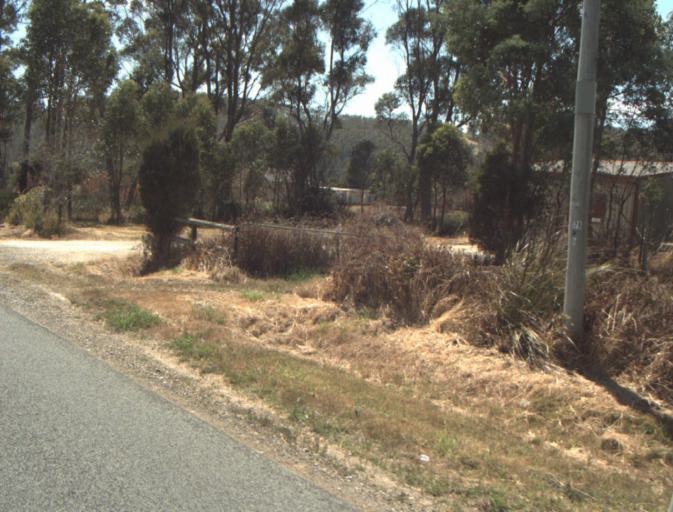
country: AU
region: Tasmania
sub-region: Launceston
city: Mayfield
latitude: -41.2554
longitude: 147.1466
